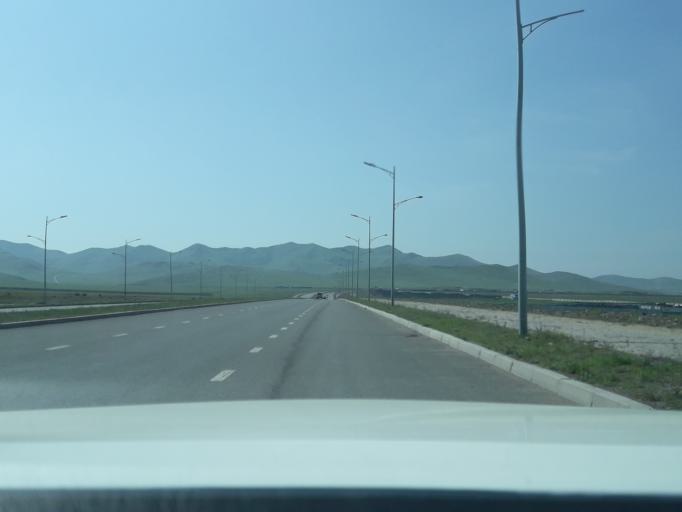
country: MN
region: Ulaanbaatar
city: Ulaanbaatar
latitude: 47.8378
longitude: 106.7891
